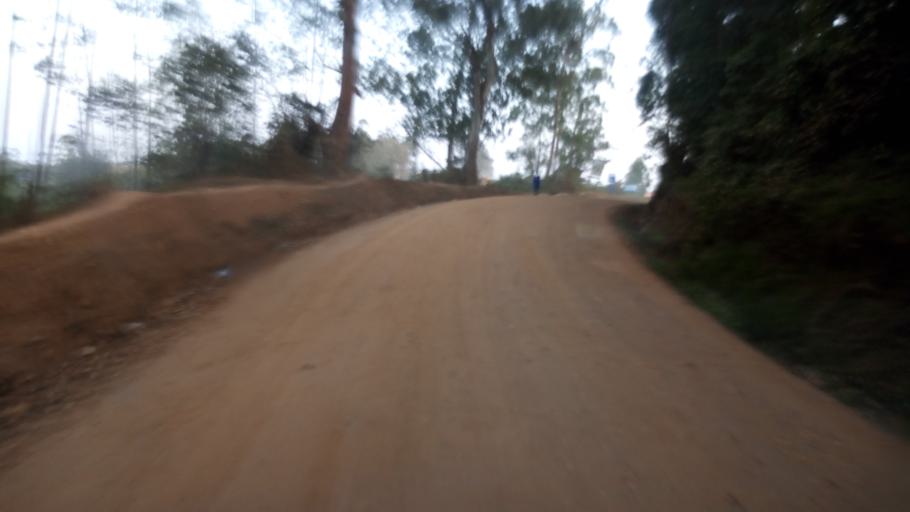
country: UG
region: Western Region
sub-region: Rukungiri District
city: Rukungiri
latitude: -0.7768
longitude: 29.9246
